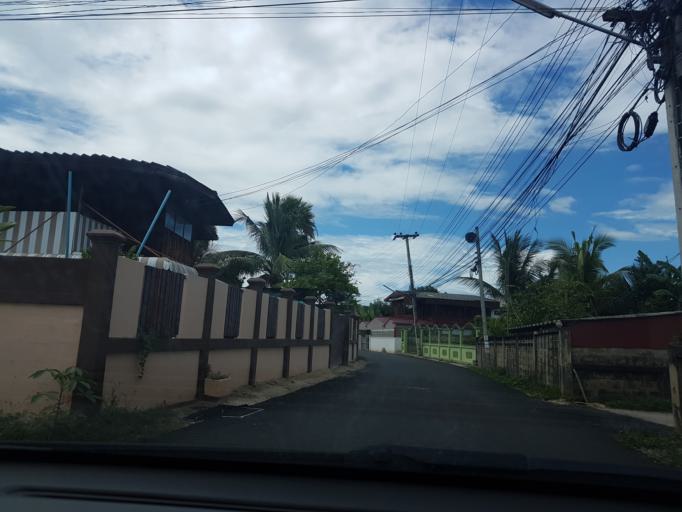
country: TH
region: Lampang
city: Ko Kha
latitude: 18.2320
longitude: 99.4210
